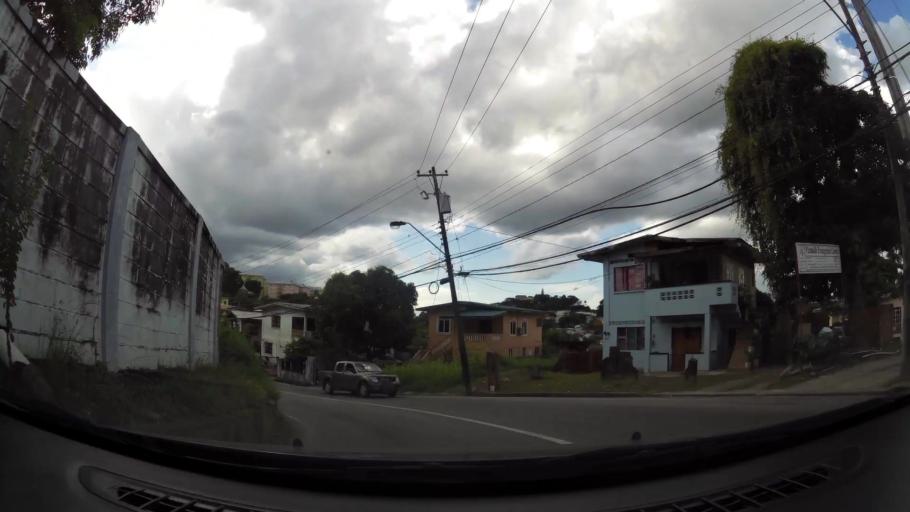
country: TT
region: City of San Fernando
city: Mon Repos
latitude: 10.2859
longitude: -61.4530
